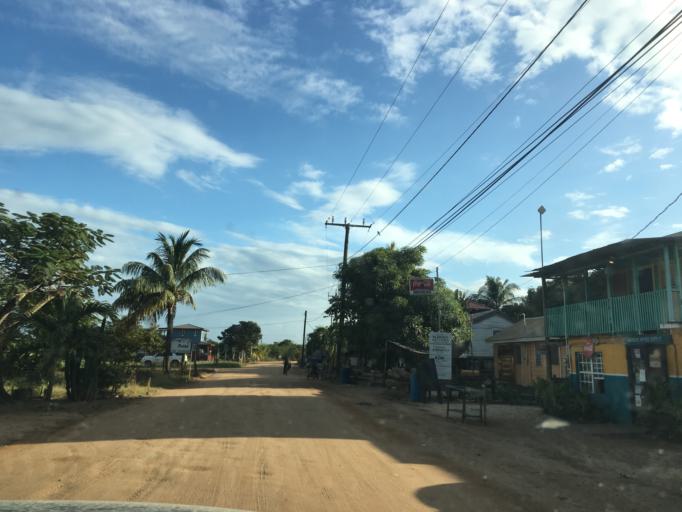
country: BZ
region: Stann Creek
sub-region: Dangriga
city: Dangriga
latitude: 16.8523
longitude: -88.2798
